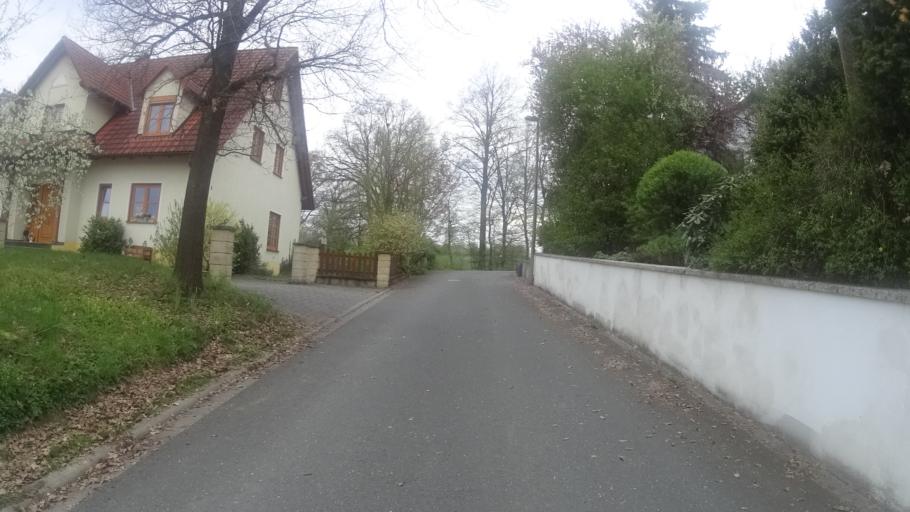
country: DE
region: Bavaria
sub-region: Upper Franconia
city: Igensdorf
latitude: 49.6039
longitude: 11.1996
